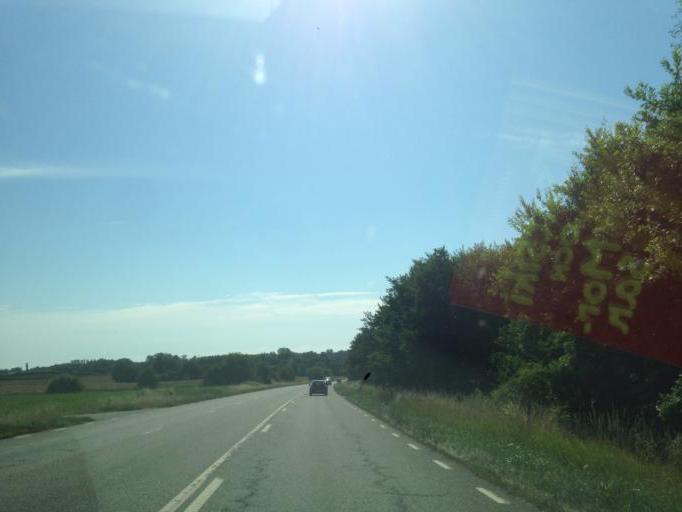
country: SE
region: Skane
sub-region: Simrishamns Kommun
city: Kivik
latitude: 55.6353
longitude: 14.2428
